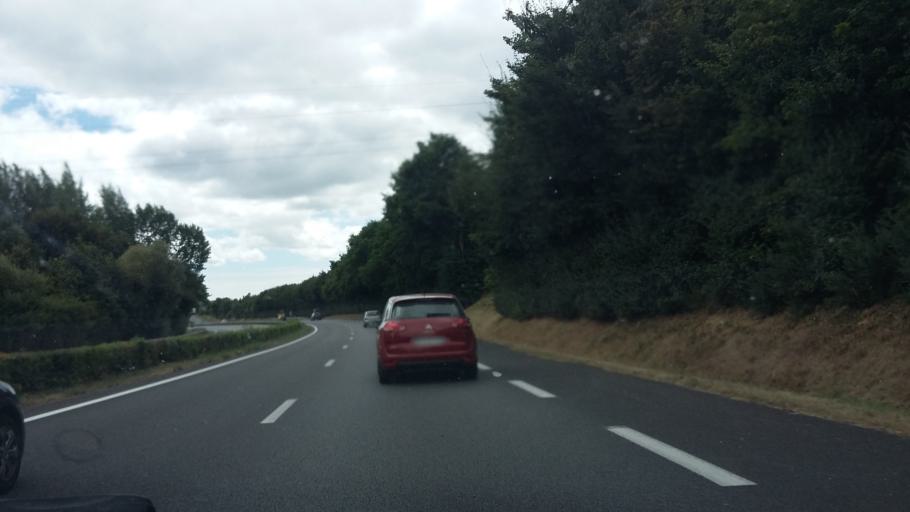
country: FR
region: Pays de la Loire
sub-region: Departement de la Vendee
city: Challans
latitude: 46.8449
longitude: -1.8525
